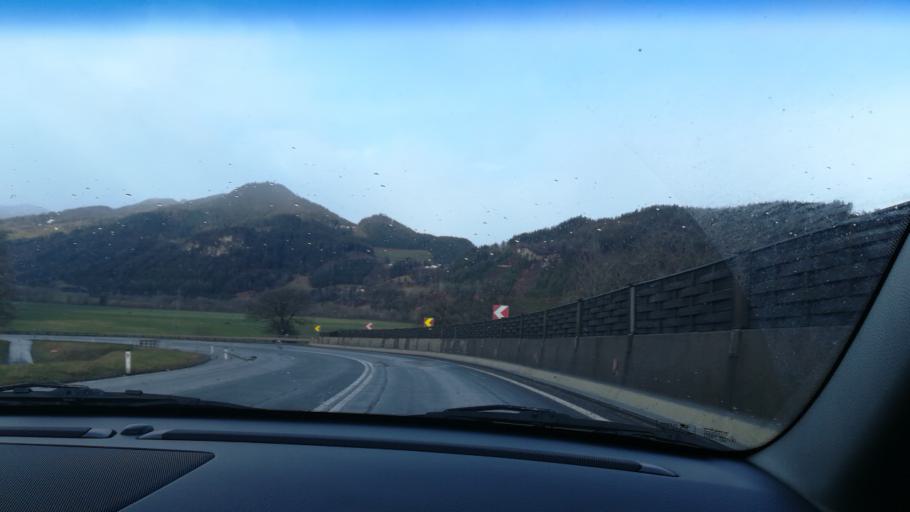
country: AT
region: Styria
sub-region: Politischer Bezirk Murtal
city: Poels
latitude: 47.2011
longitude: 14.5684
